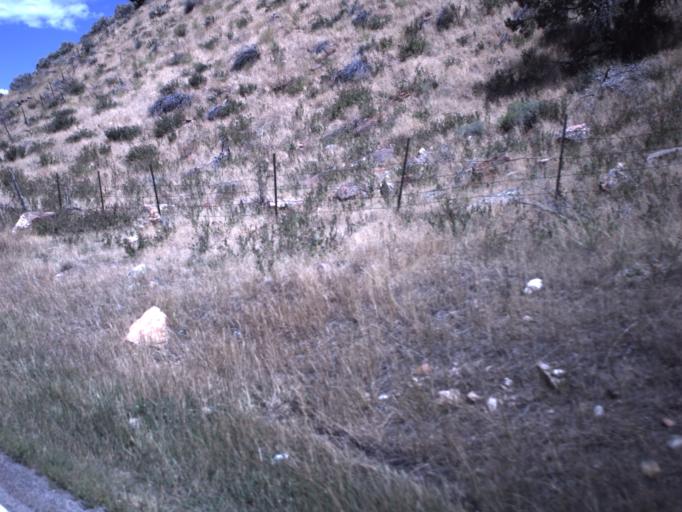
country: US
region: Utah
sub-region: Summit County
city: Oakley
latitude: 40.7323
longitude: -111.3480
